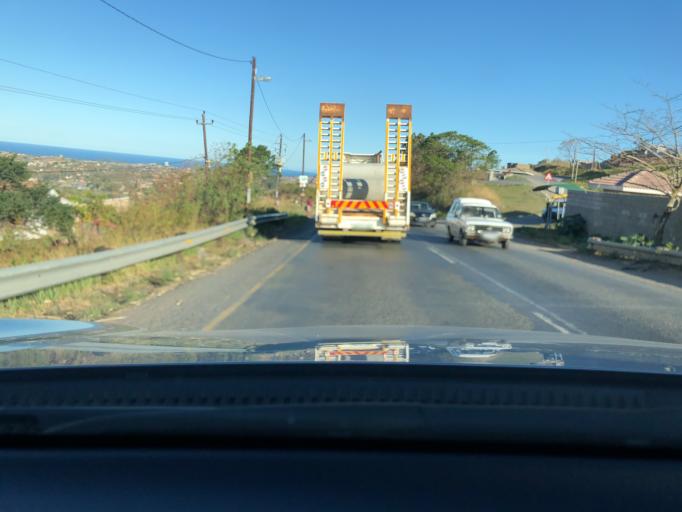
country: ZA
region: KwaZulu-Natal
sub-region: eThekwini Metropolitan Municipality
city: Umkomaas
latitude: -30.0198
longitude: 30.8094
